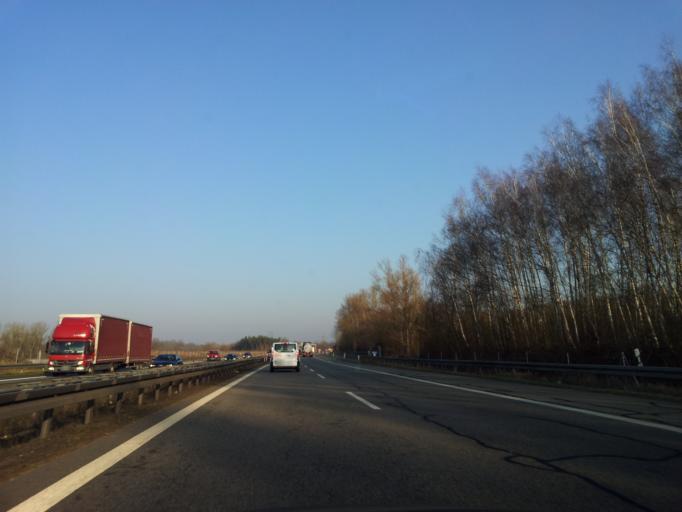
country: FR
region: Alsace
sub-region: Departement du Haut-Rhin
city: Rosenau
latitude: 47.6503
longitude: 7.5405
